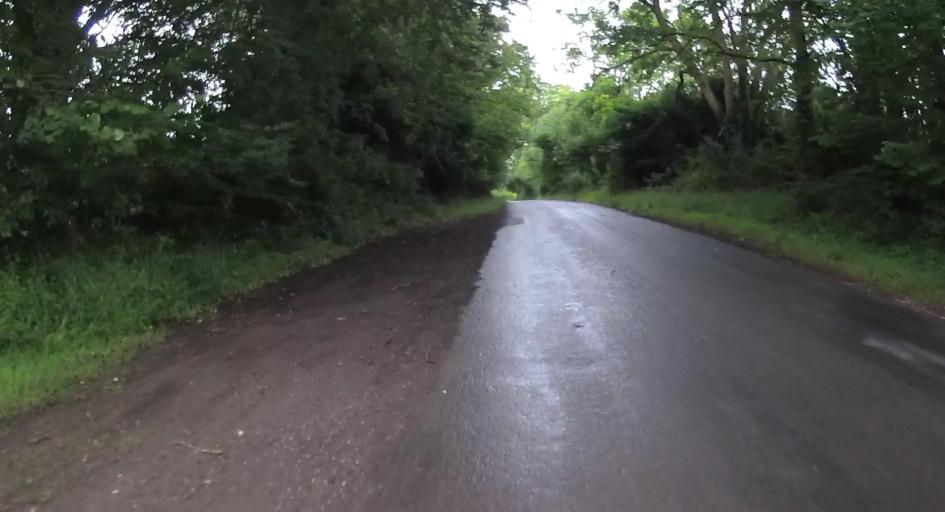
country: GB
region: England
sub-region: Hampshire
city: Andover
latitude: 51.2098
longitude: -1.4324
